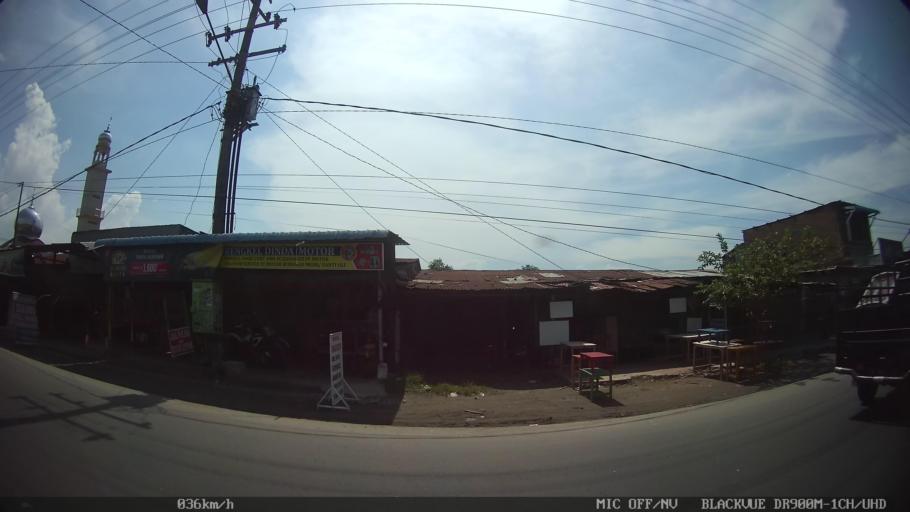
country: ID
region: North Sumatra
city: Medan
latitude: 3.6421
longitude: 98.6577
